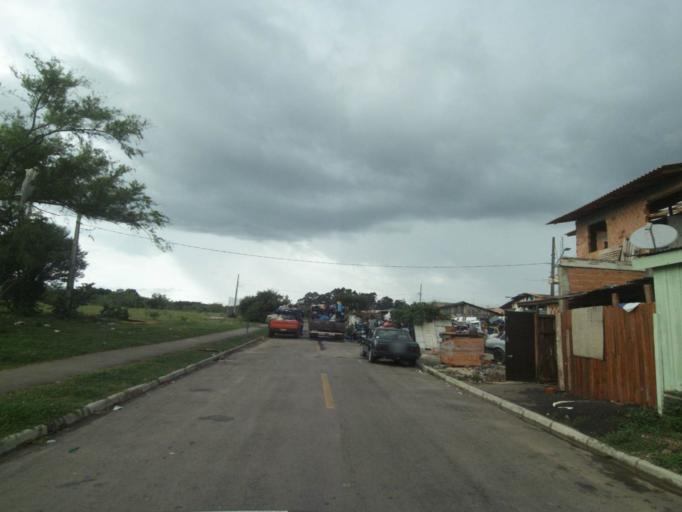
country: BR
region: Parana
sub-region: Pinhais
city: Pinhais
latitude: -25.4687
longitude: -49.1886
